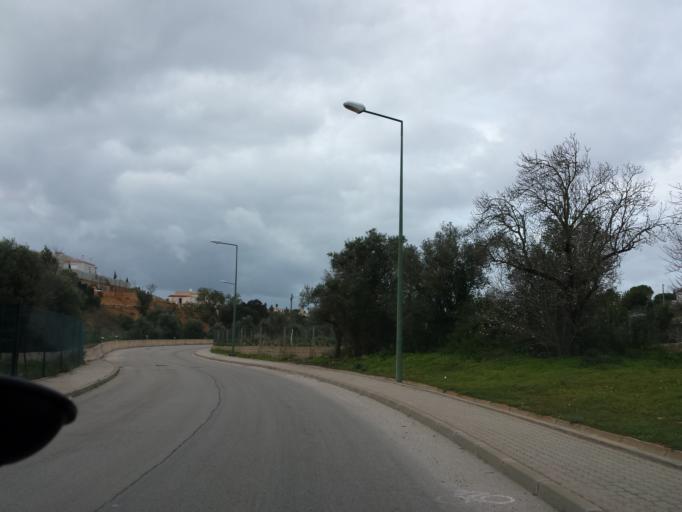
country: PT
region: Faro
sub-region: Lagoa
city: Estombar
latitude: 37.1332
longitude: -8.4836
